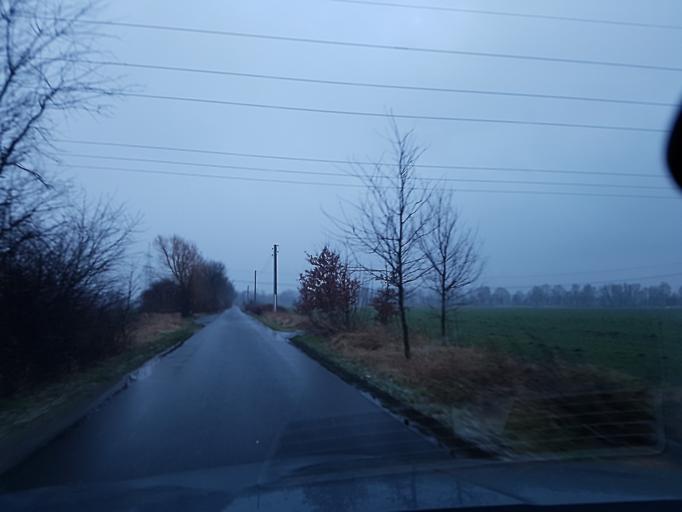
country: DE
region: Brandenburg
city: Groden
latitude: 51.4340
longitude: 13.5553
